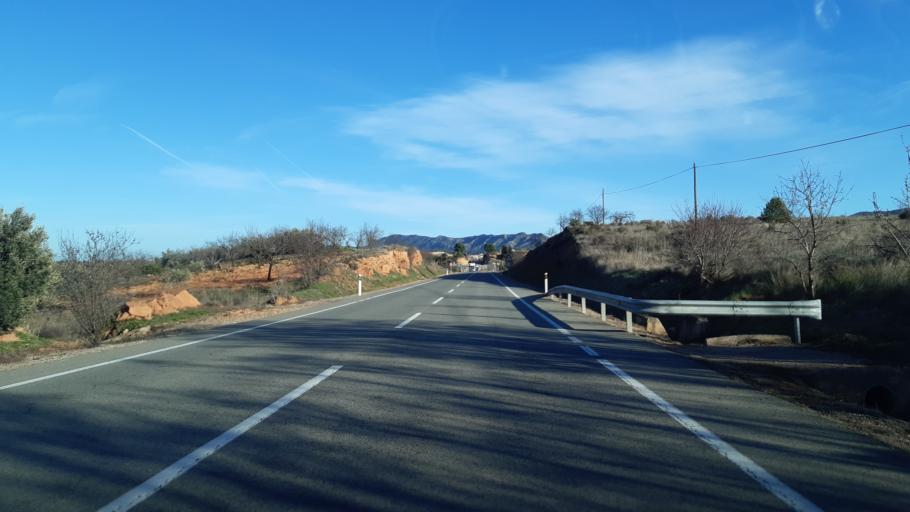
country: ES
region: Catalonia
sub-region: Provincia de Tarragona
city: Gandesa
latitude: 41.0543
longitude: 0.4222
